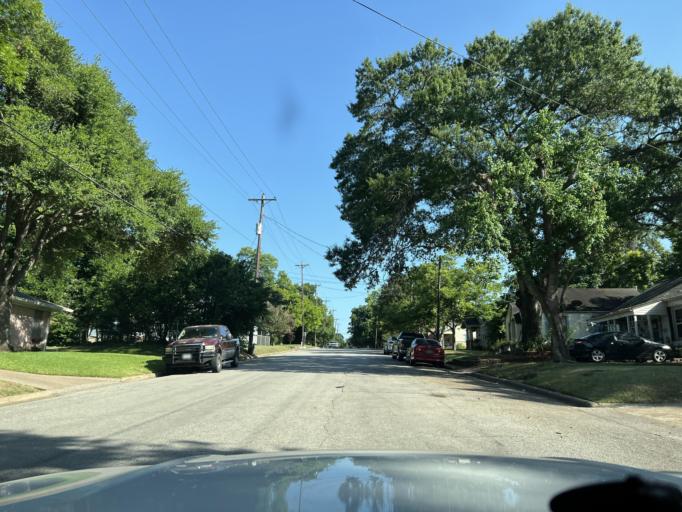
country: US
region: Texas
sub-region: Washington County
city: Brenham
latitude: 30.1544
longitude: -96.3966
